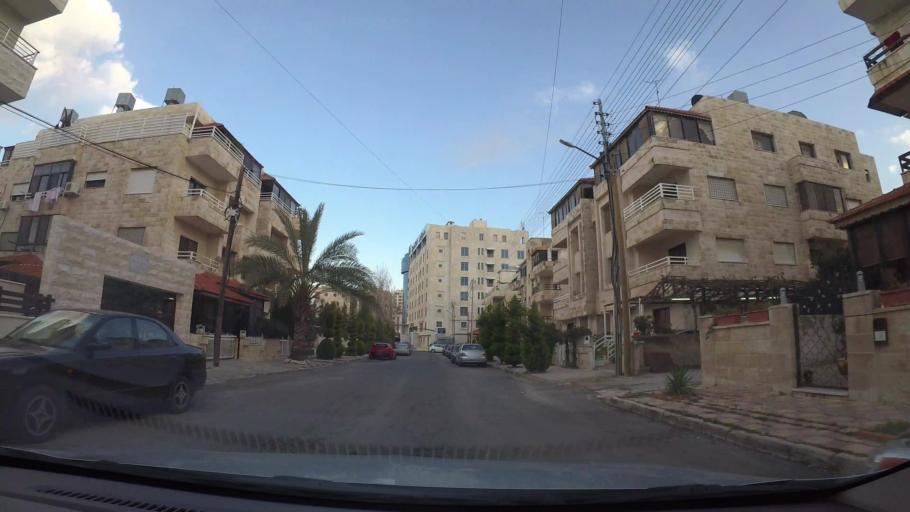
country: JO
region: Amman
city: Al Jubayhah
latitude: 31.9828
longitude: 35.8632
